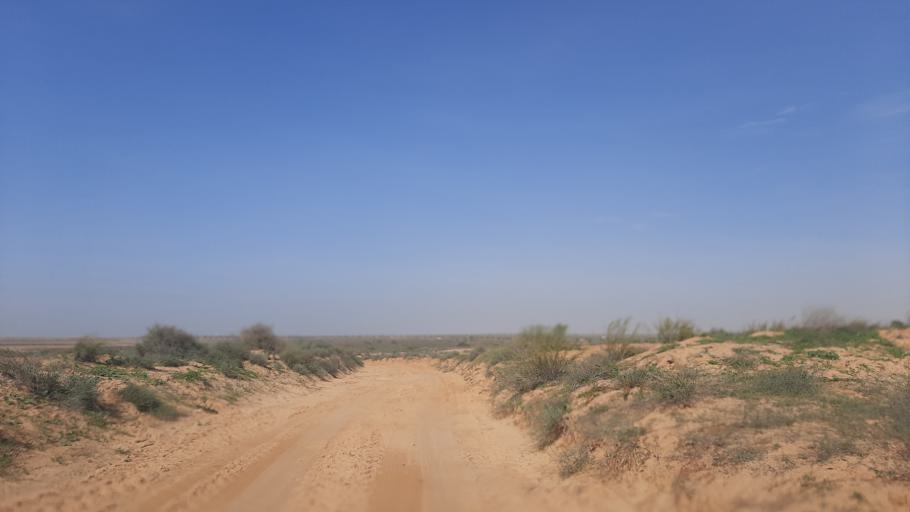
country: TN
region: Madanin
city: Zarzis
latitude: 33.4389
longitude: 10.8070
